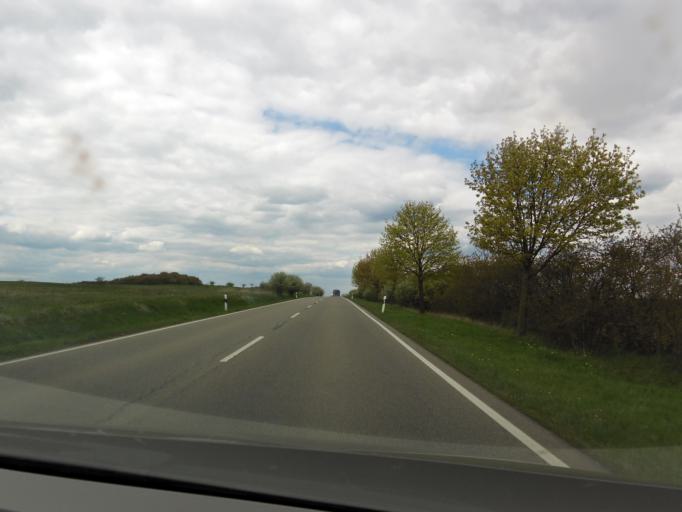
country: DE
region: Saxony-Anhalt
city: Eckartsberga
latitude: 51.1169
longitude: 11.5895
